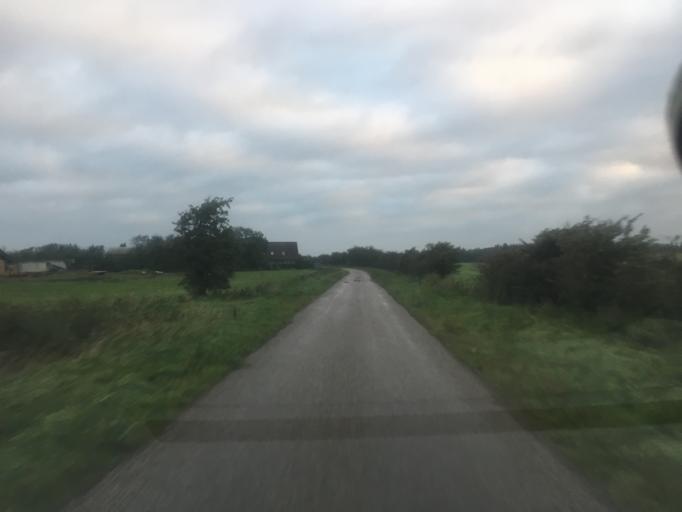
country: DK
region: South Denmark
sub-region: Tonder Kommune
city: Logumkloster
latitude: 54.9854
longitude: 8.9317
